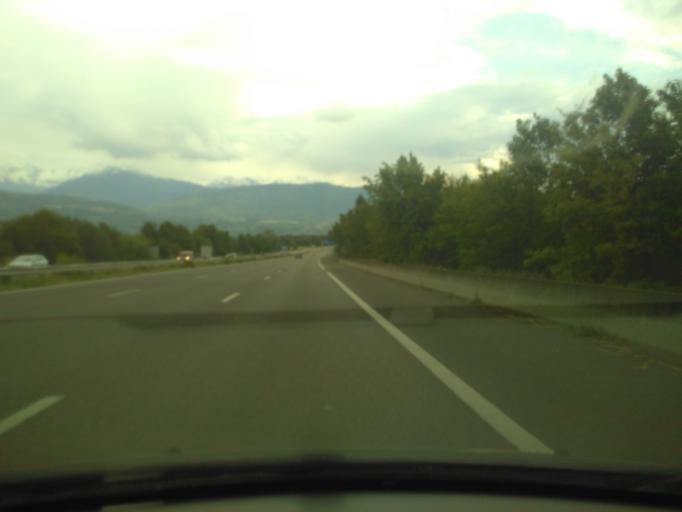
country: FR
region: Rhone-Alpes
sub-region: Departement de la Savoie
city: Les Marches
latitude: 45.4977
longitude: 6.0204
